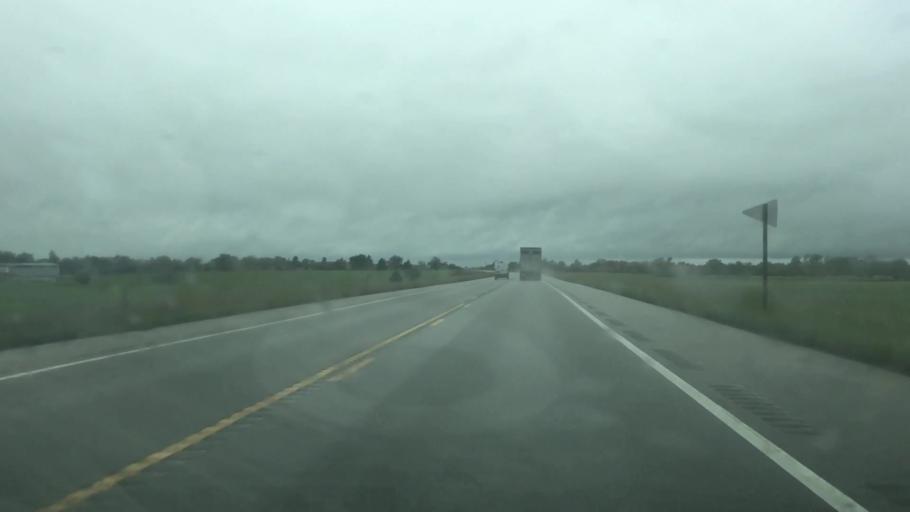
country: US
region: Kansas
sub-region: Allen County
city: Iola
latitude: 38.0794
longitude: -95.3721
